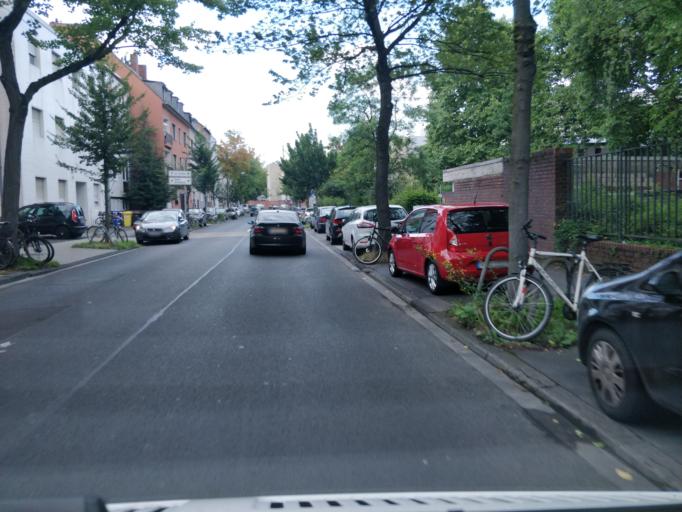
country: DE
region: North Rhine-Westphalia
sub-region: Regierungsbezirk Koln
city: Neustadt/Sued
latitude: 50.9249
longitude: 6.9143
